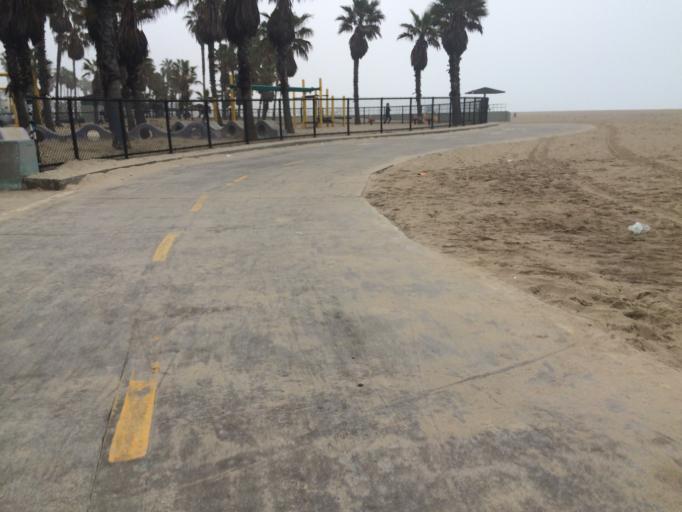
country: US
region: California
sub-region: Los Angeles County
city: Santa Monica
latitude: 33.9949
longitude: -118.4816
